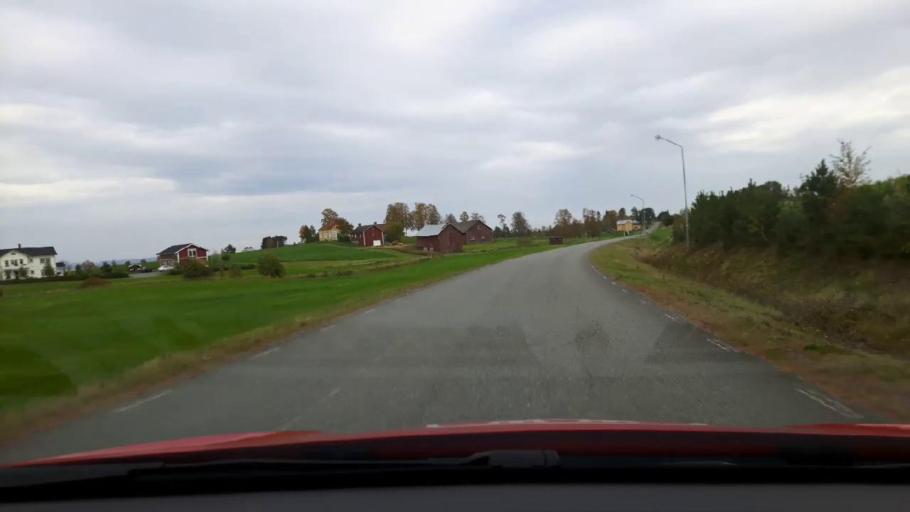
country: SE
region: Jaemtland
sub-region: Krokoms Kommun
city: Krokom
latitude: 63.2348
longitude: 14.1201
